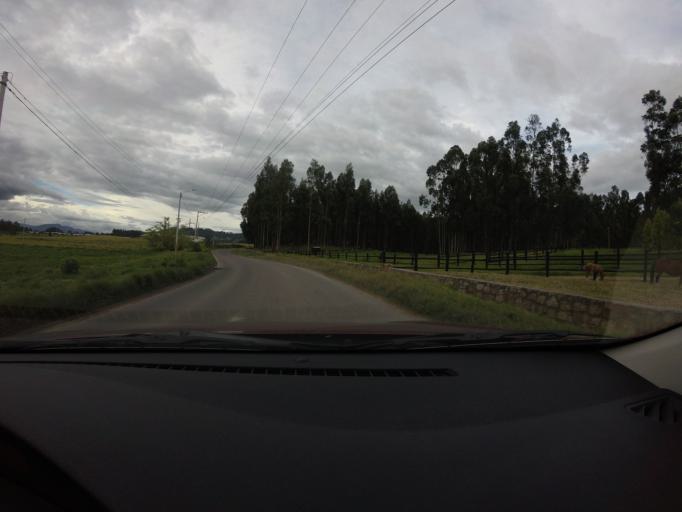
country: CO
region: Cundinamarca
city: Cajica
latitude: 4.9214
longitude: -74.0051
